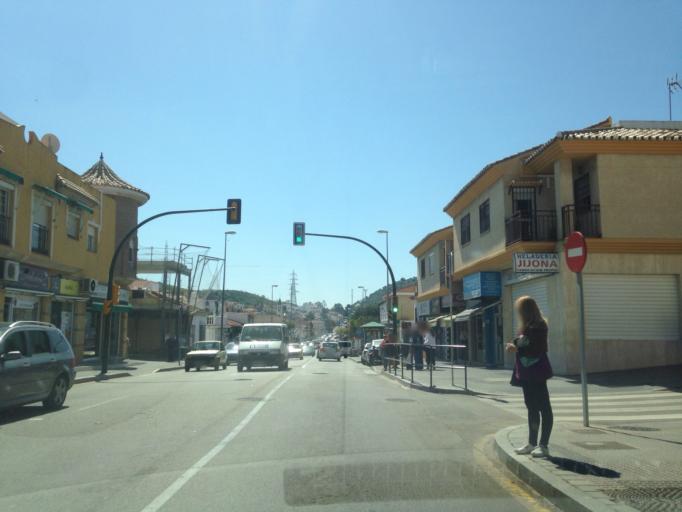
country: ES
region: Andalusia
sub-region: Provincia de Malaga
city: Malaga
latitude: 36.7394
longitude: -4.4816
